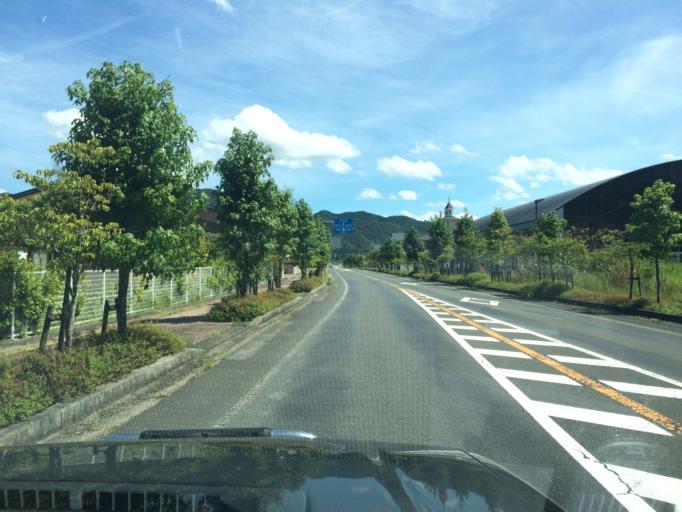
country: JP
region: Hyogo
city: Toyooka
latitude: 35.4680
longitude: 134.8570
